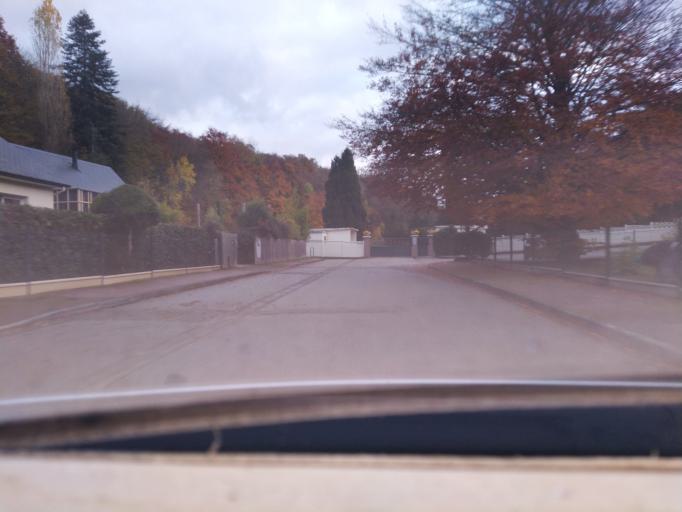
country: FR
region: Haute-Normandie
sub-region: Departement de la Seine-Maritime
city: Yainville
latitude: 49.4527
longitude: 0.8324
